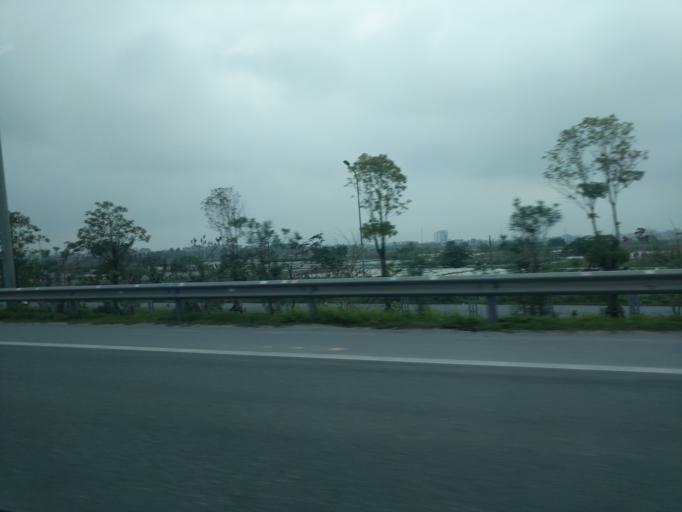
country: VN
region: Ha Noi
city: Dong Anh
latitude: 21.1490
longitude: 105.8194
